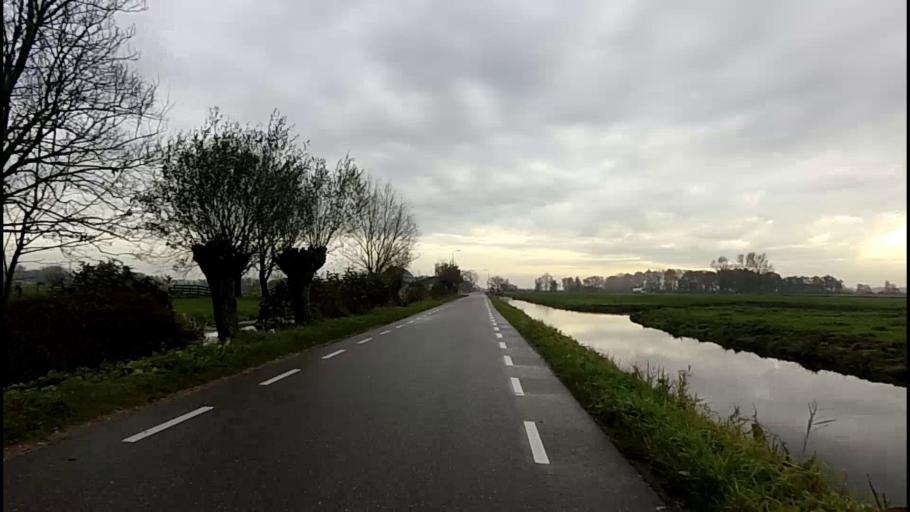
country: NL
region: South Holland
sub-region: Molenwaard
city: Nieuw-Lekkerland
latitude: 51.9195
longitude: 4.6564
